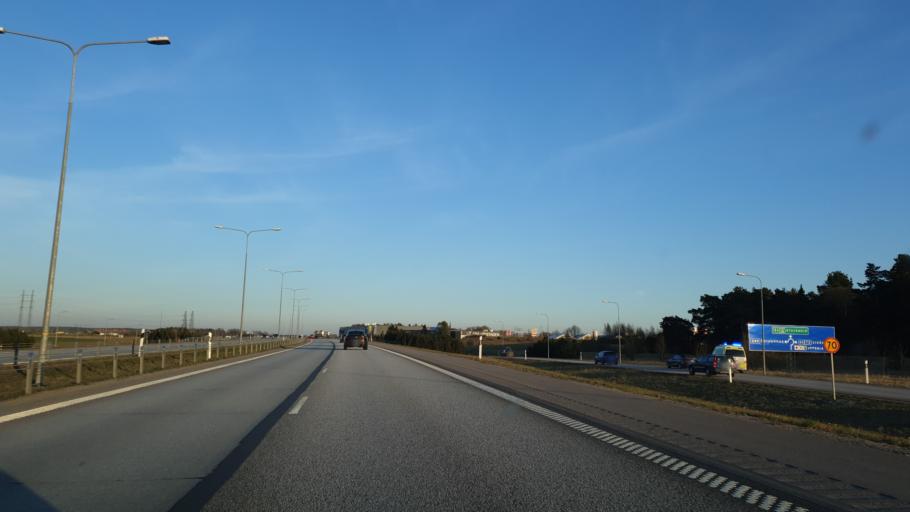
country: SE
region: Uppsala
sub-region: Uppsala Kommun
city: Gamla Uppsala
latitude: 59.8904
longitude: 17.6643
